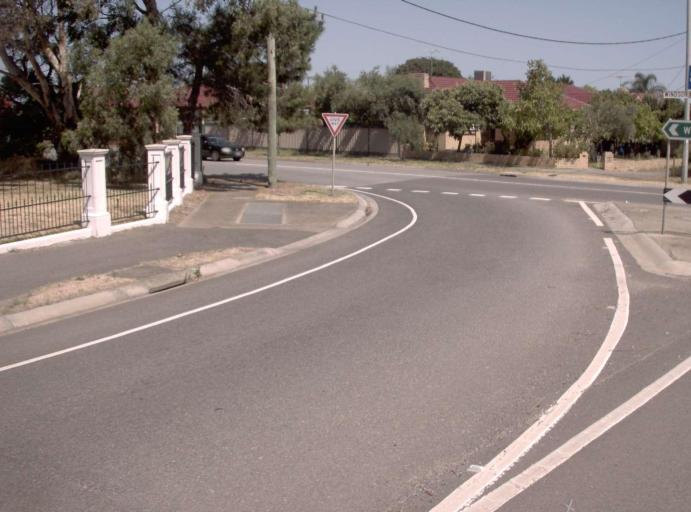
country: AU
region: Victoria
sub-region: Greater Dandenong
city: Springvale
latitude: -37.9500
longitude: 145.1387
